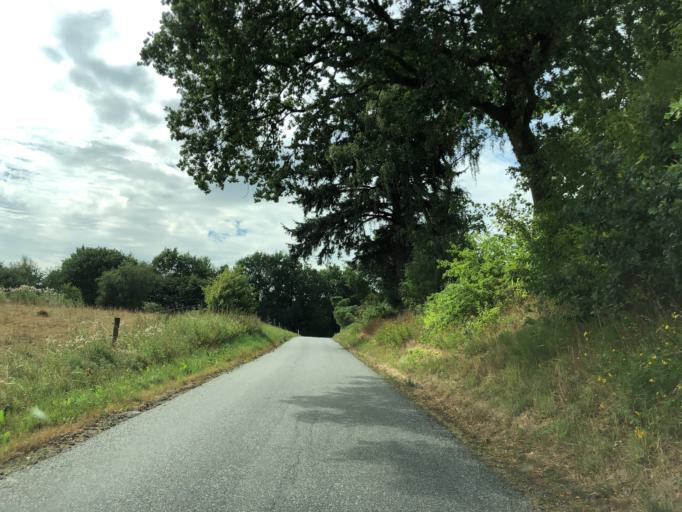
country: DK
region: South Denmark
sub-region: Vejle Kommune
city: Egtved
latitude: 55.6436
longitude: 9.2540
